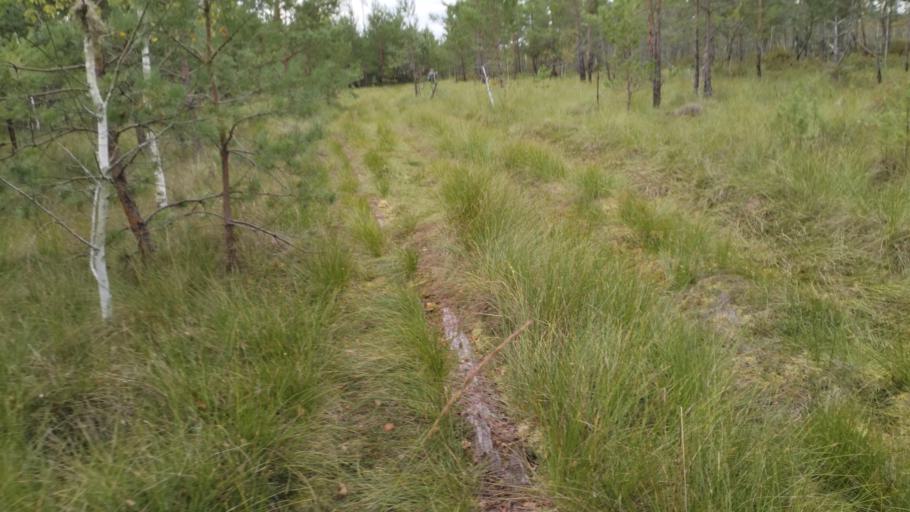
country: BY
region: Brest
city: Davyd-Haradok
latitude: 51.8949
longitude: 27.2134
